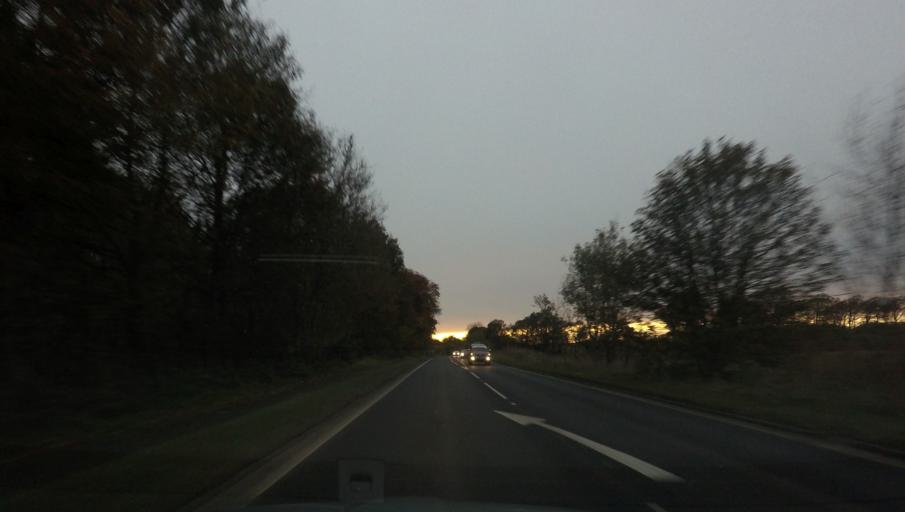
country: GB
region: Scotland
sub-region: Fife
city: Crossford
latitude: 56.0449
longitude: -3.4983
